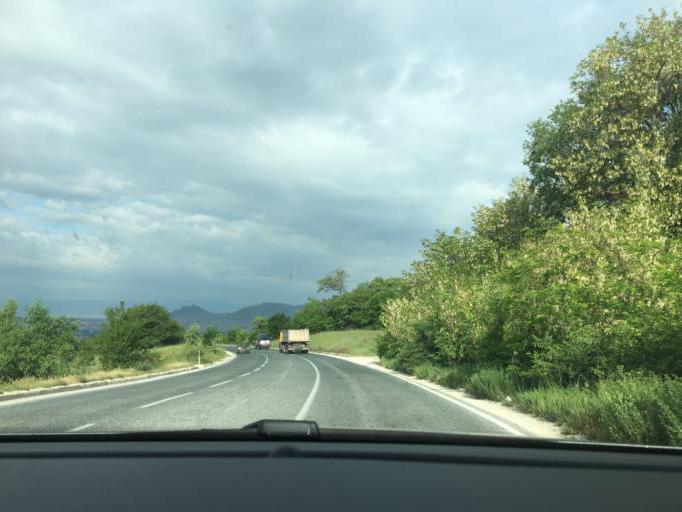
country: MK
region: Prilep
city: Prilep
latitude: 41.3693
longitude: 21.6337
